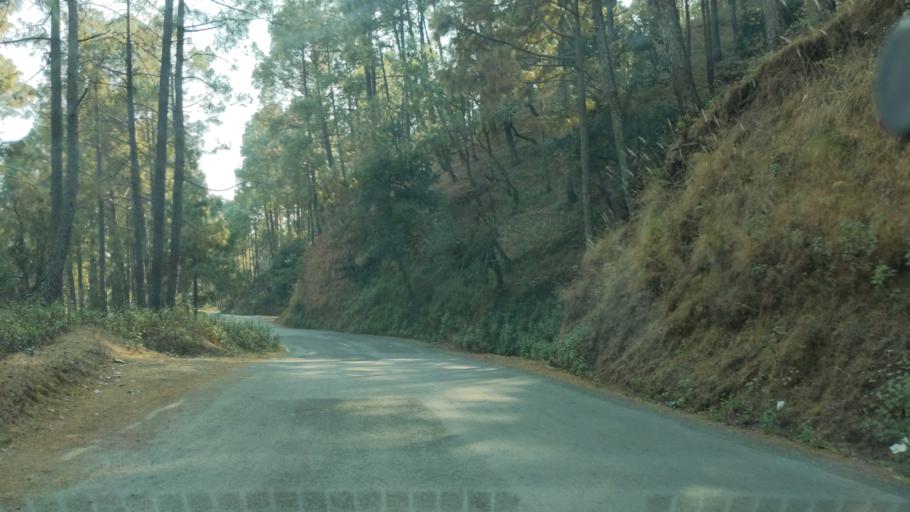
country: IN
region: Uttarakhand
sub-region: Naini Tal
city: Bhowali
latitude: 29.3924
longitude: 79.5392
